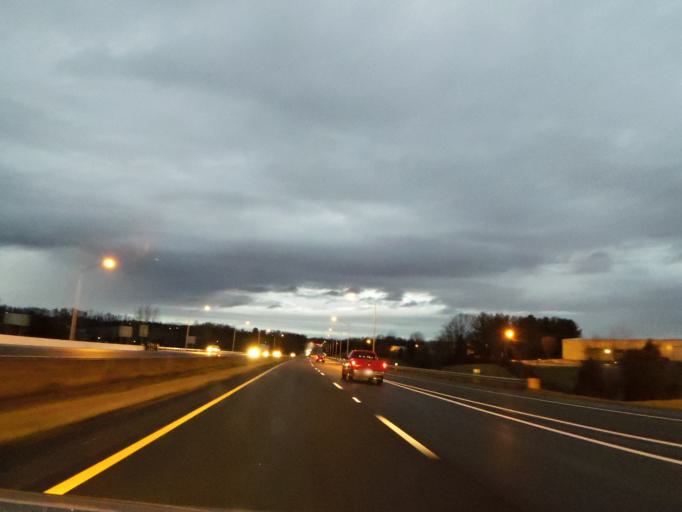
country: US
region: Tennessee
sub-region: Washington County
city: Gray
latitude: 36.4083
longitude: -82.4801
